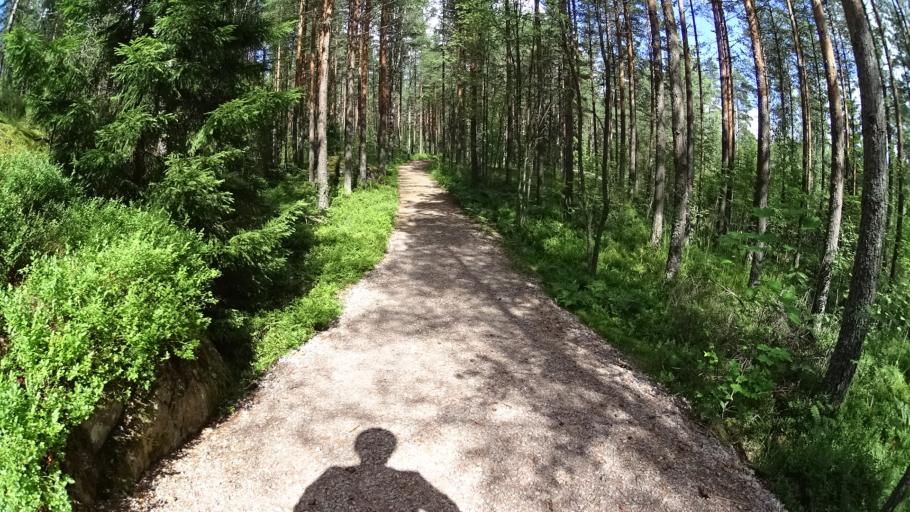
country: FI
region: Uusimaa
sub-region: Helsinki
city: Kauniainen
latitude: 60.3185
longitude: 24.6815
